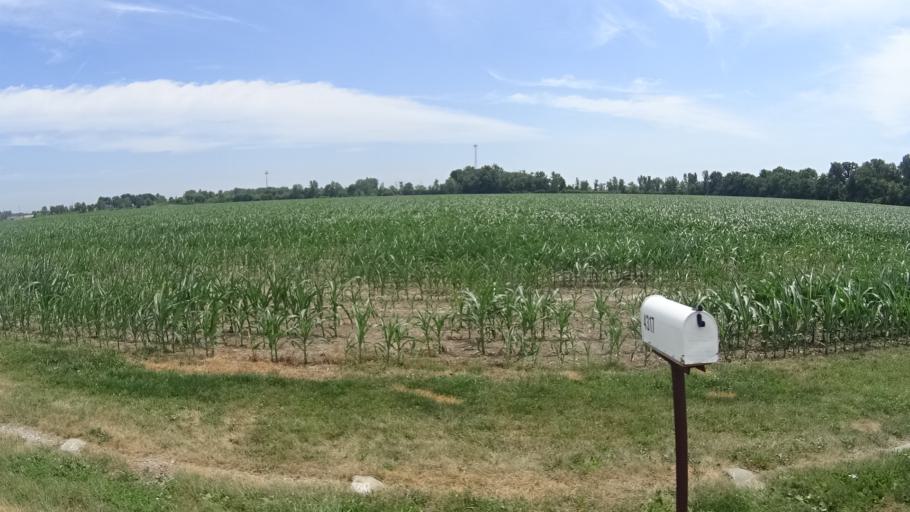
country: US
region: Ohio
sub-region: Erie County
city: Sandusky
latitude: 41.4278
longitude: -82.7610
